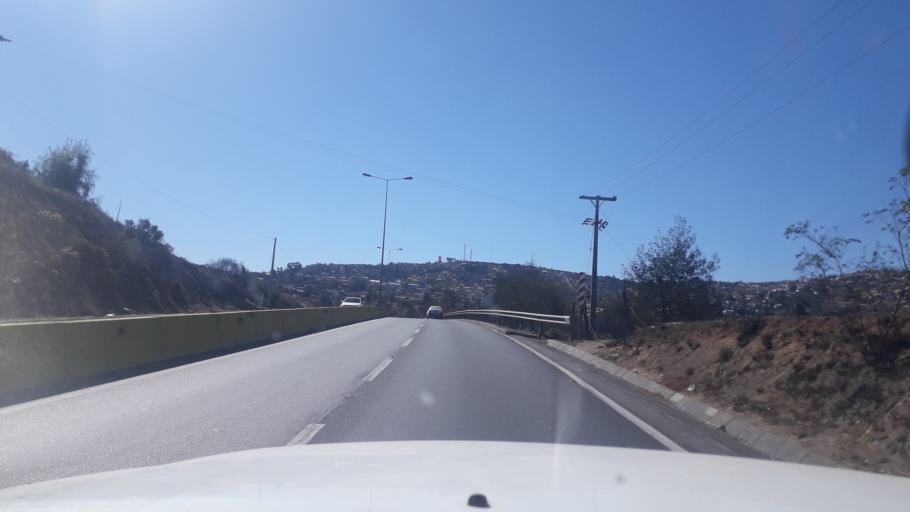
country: CL
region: Valparaiso
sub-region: Provincia de Valparaiso
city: Vina del Mar
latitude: -33.0298
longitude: -71.4998
